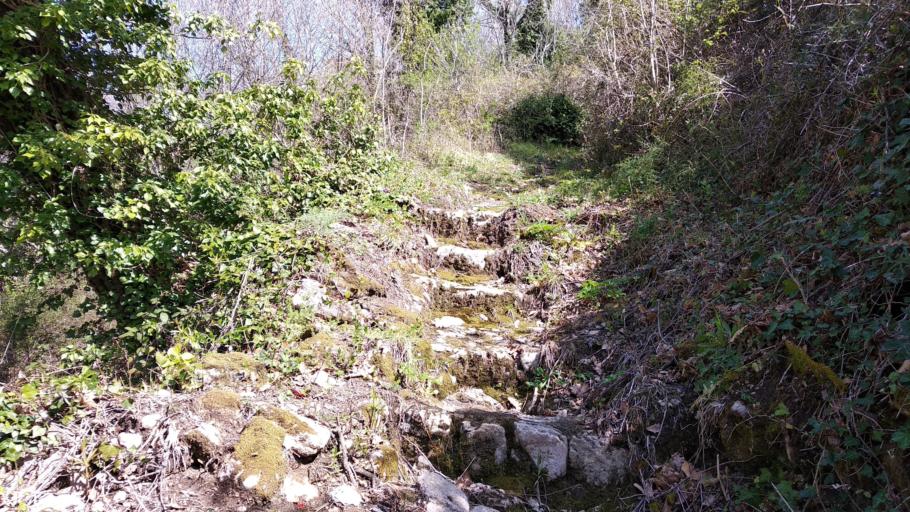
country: IT
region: Calabria
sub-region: Provincia di Cosenza
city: Altilia
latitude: 39.1302
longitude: 16.2500
